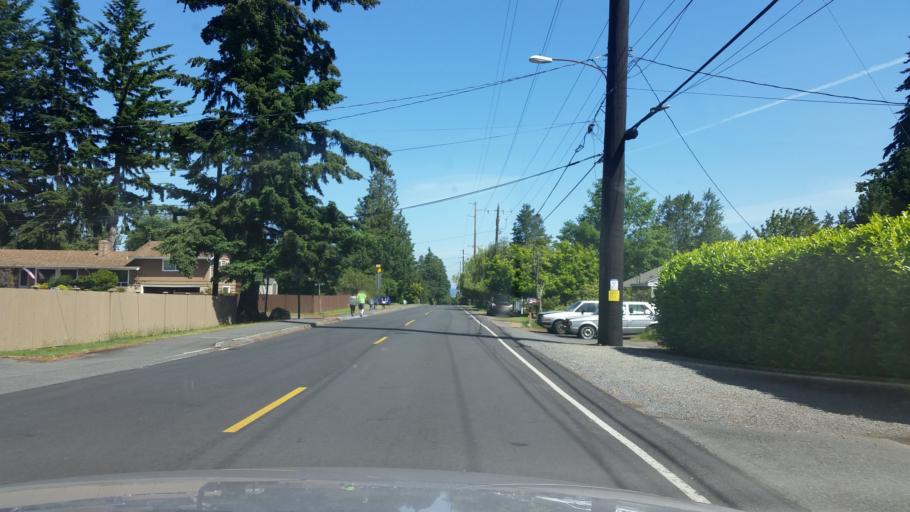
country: US
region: Washington
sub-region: Snohomish County
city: Esperance
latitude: 47.8000
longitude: -122.3615
